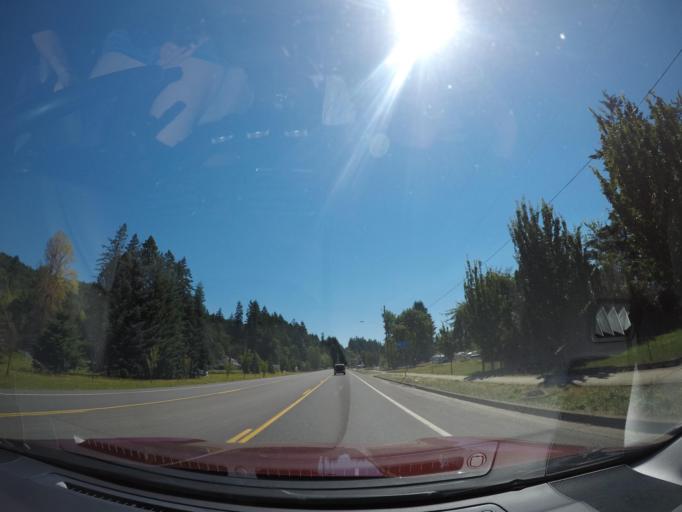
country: US
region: Oregon
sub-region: Linn County
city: Mill City
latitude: 44.7573
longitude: -122.4860
